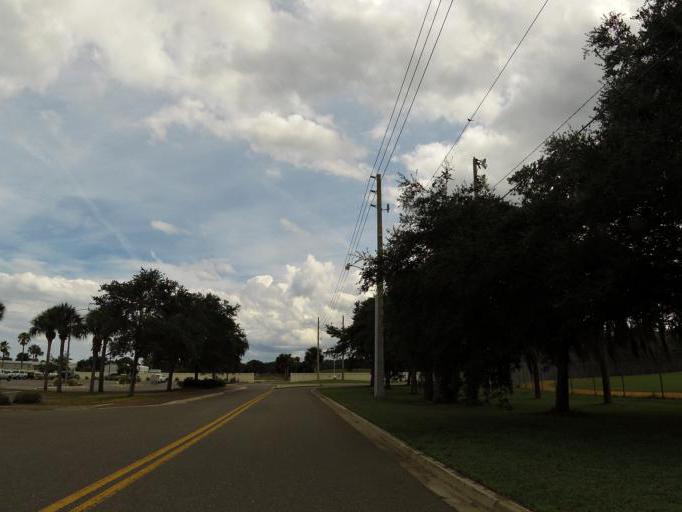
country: US
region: Florida
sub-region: Duval County
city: Jacksonville Beach
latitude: 30.2830
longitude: -81.4046
